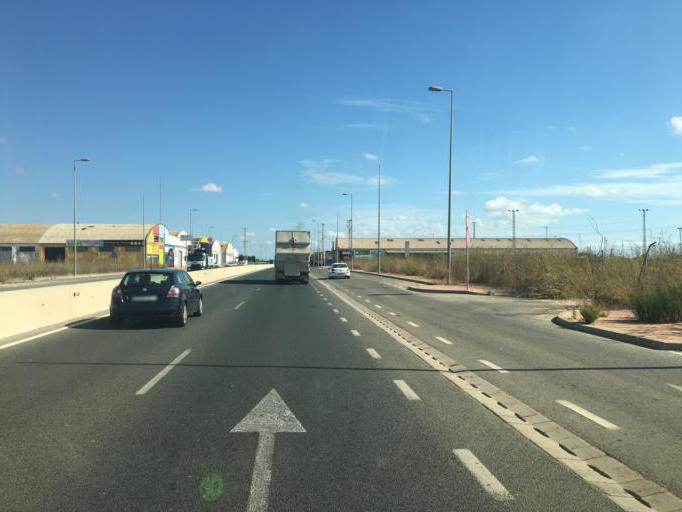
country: ES
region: Murcia
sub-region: Murcia
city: Cartagena
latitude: 37.6468
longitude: -0.9855
